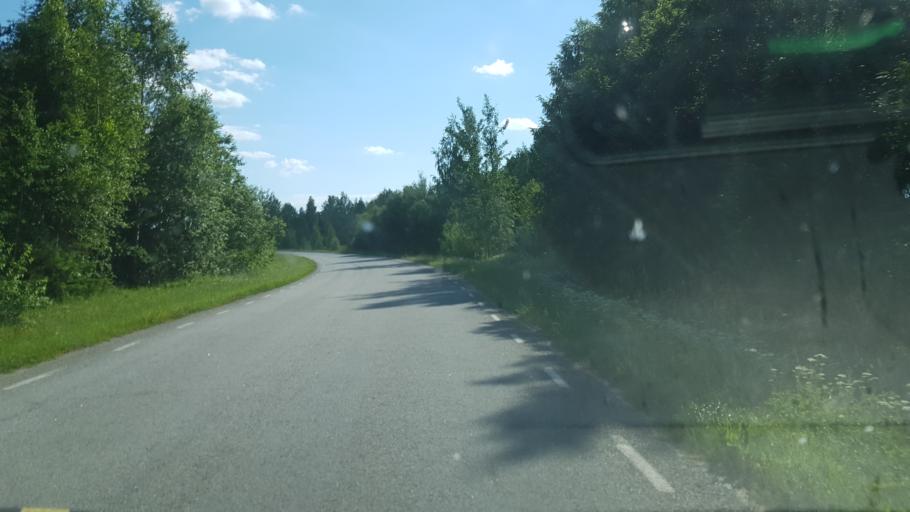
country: EE
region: Vorumaa
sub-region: Voru linn
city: Voru
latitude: 57.7869
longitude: 26.9495
